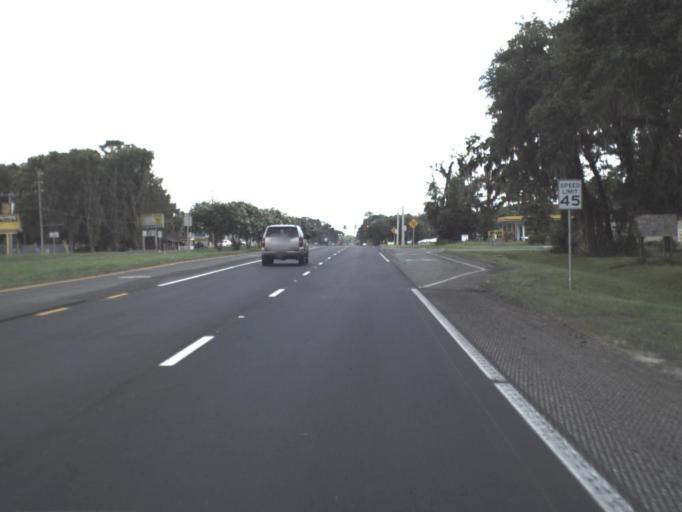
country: US
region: Florida
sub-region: Columbia County
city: Lake City
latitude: 30.1474
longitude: -82.6400
